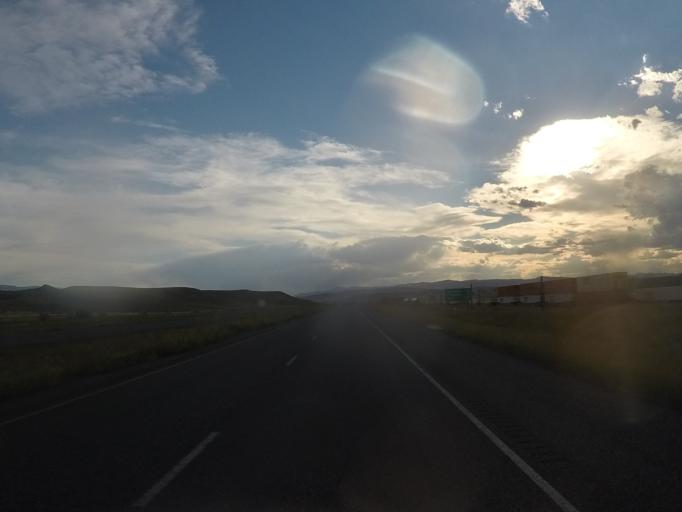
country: US
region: Montana
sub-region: Park County
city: Livingston
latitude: 45.7134
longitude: -110.4147
